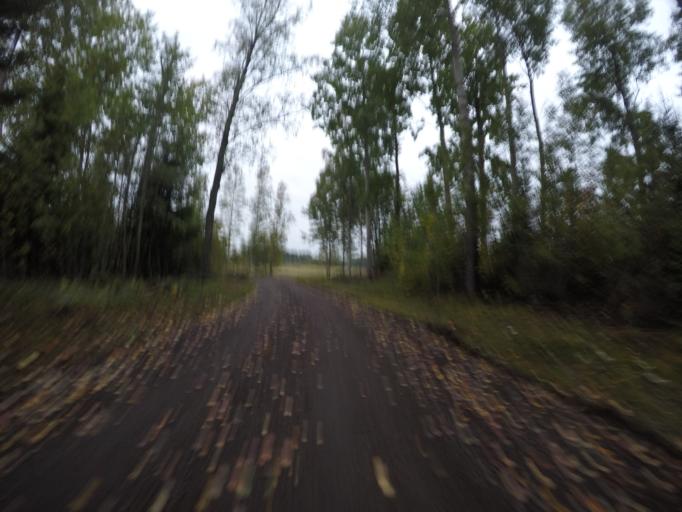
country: SE
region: Vaestmanland
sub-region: Kungsors Kommun
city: Kungsoer
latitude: 59.3994
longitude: 16.1158
